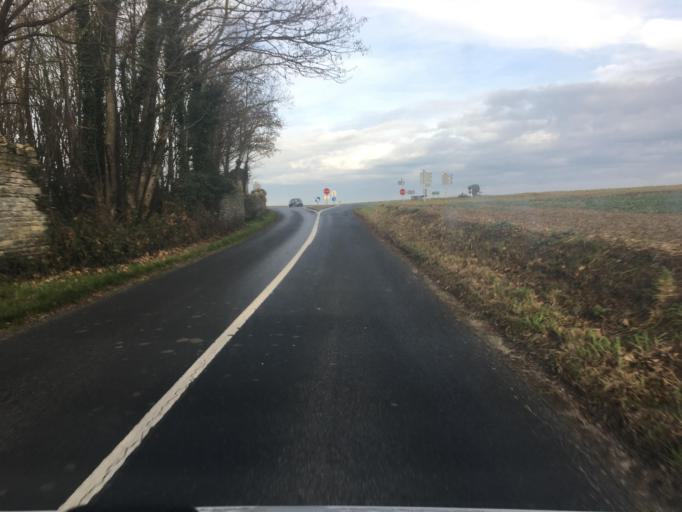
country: FR
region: Lower Normandy
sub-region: Departement du Calvados
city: Creully
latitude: 49.2926
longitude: -0.5431
